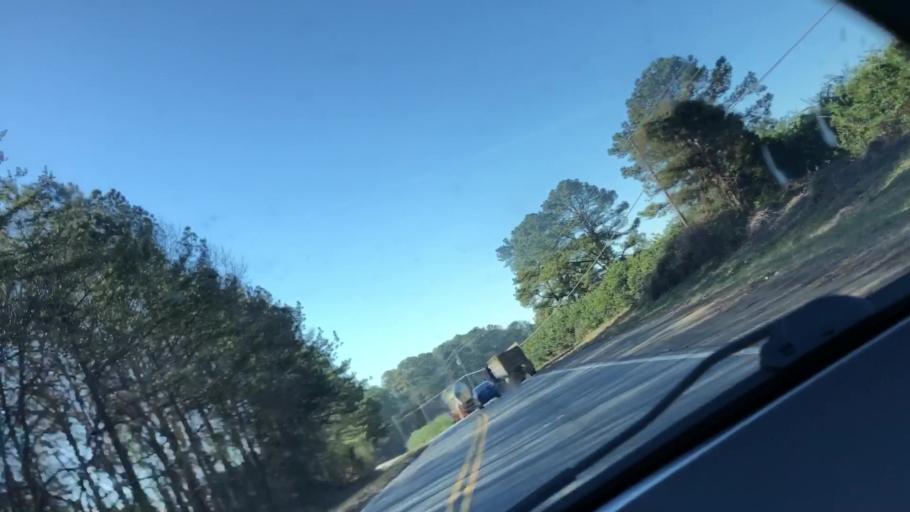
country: US
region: Georgia
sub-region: Bartow County
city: Cartersville
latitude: 34.2189
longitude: -84.8017
